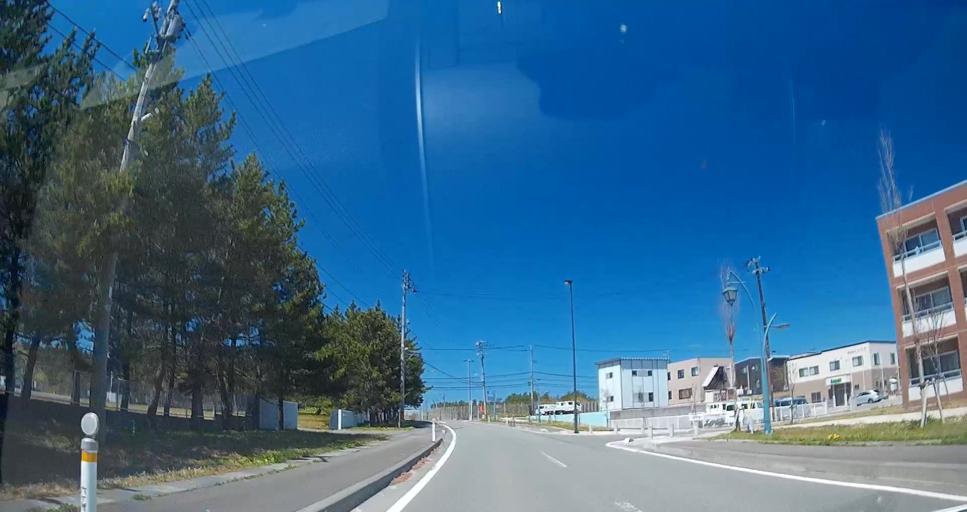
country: JP
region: Aomori
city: Misawa
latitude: 40.9699
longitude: 141.3606
